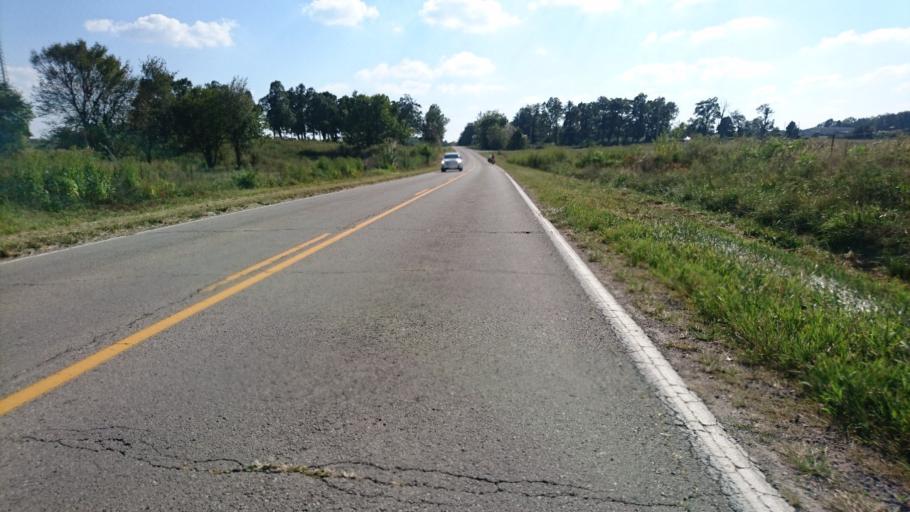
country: US
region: Missouri
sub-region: Laclede County
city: Lebanon
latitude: 37.6281
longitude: -92.6891
